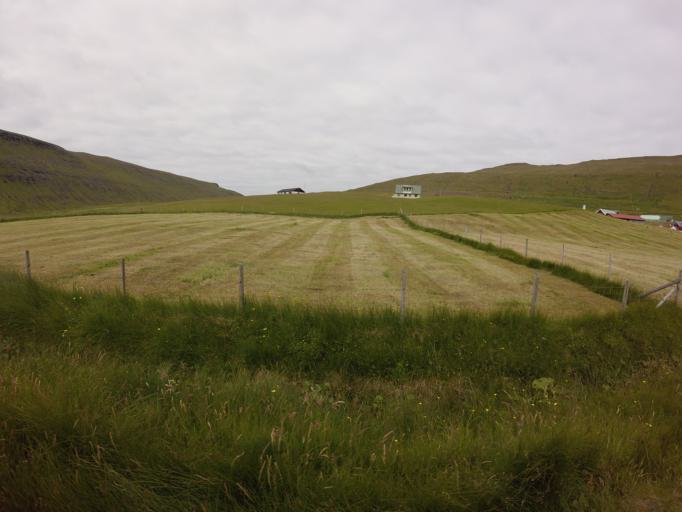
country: FO
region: Suduroy
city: Tvoroyri
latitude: 61.6301
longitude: -6.9300
